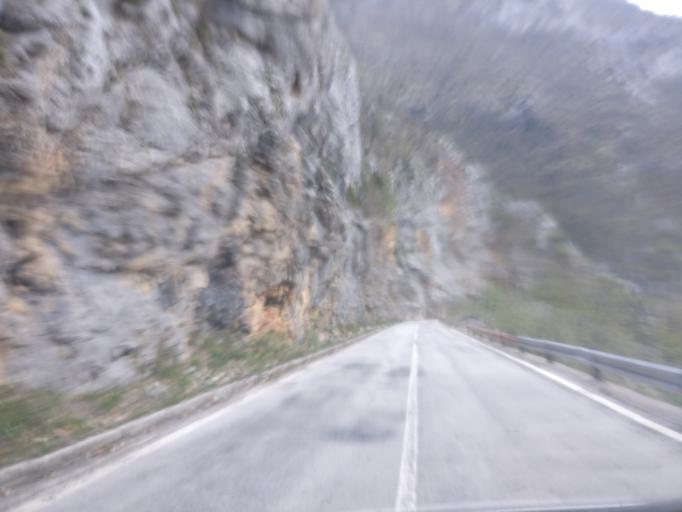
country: ME
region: Opstina Pluzine
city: Pluzine
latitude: 43.2435
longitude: 18.8379
